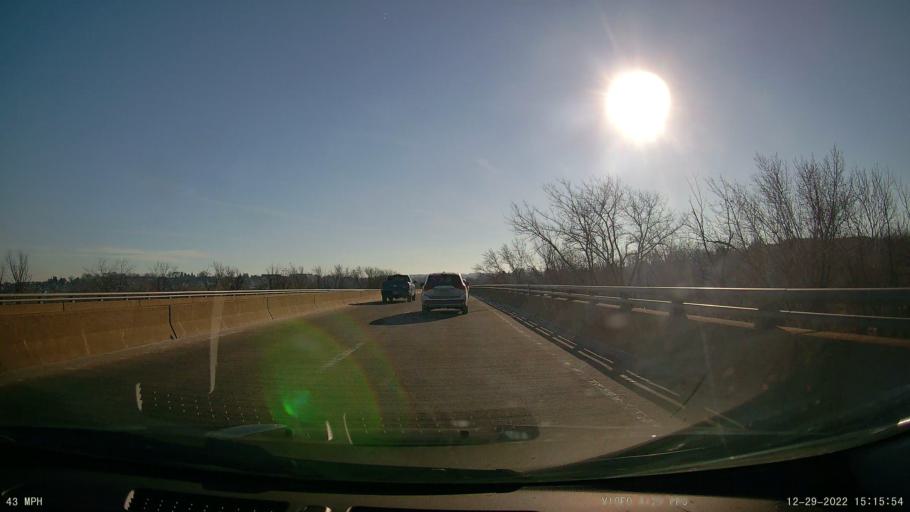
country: US
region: Pennsylvania
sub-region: Montgomery County
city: Bridgeport
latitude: 40.1121
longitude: -75.3501
